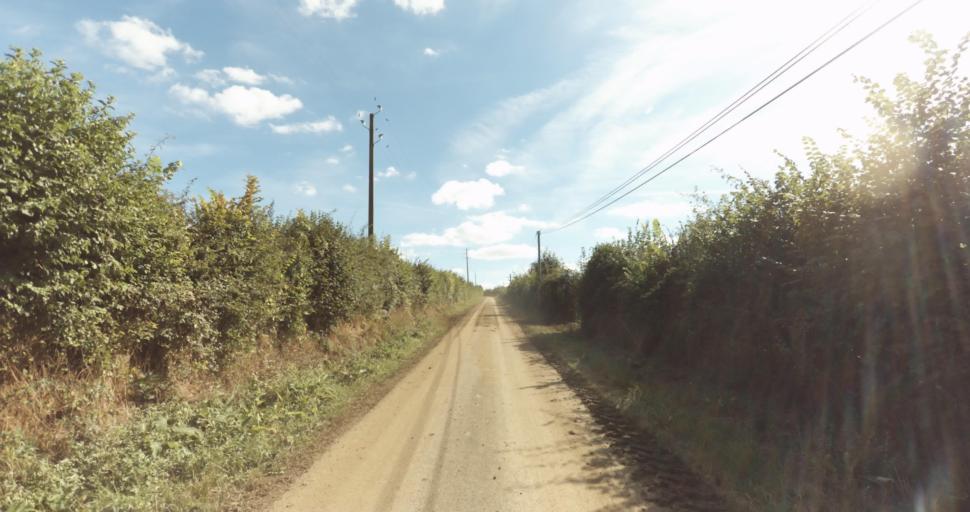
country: FR
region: Lower Normandy
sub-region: Departement de l'Orne
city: Vimoutiers
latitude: 48.9347
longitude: 0.1303
